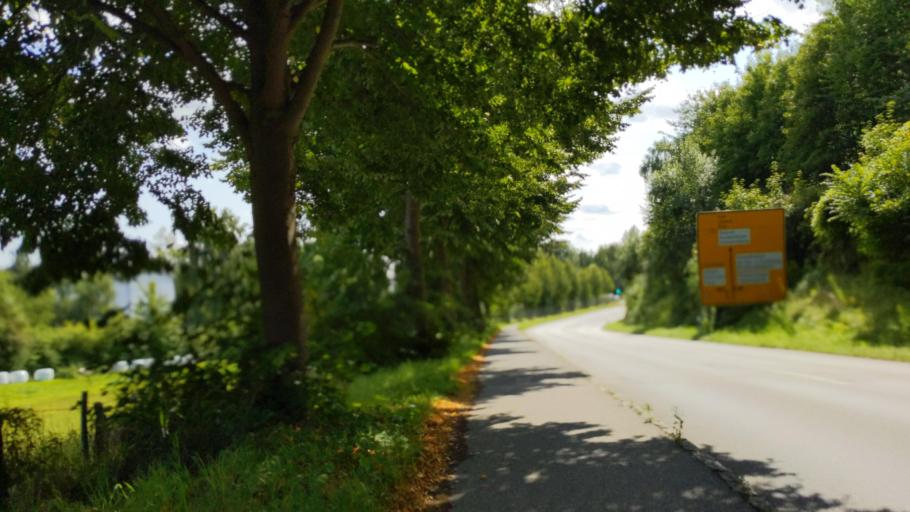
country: DE
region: Schleswig-Holstein
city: Eutin
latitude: 54.1521
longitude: 10.6048
